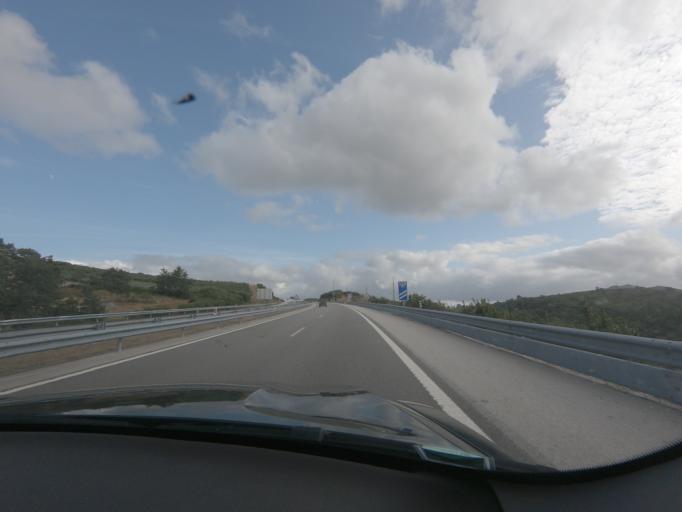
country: PT
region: Viseu
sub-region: Tarouca
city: Tarouca
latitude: 41.0121
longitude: -7.8844
